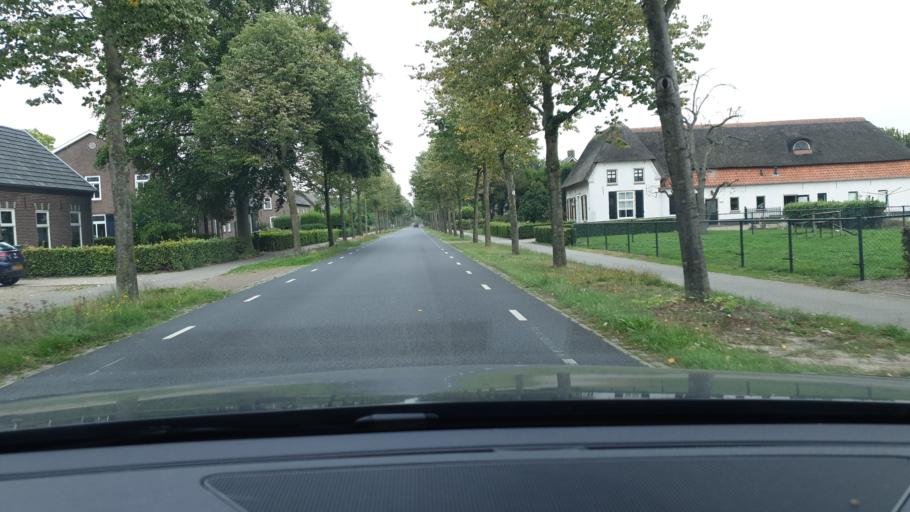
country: NL
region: North Brabant
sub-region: Gemeente Landerd
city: Schaijk
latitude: 51.7459
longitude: 5.6419
